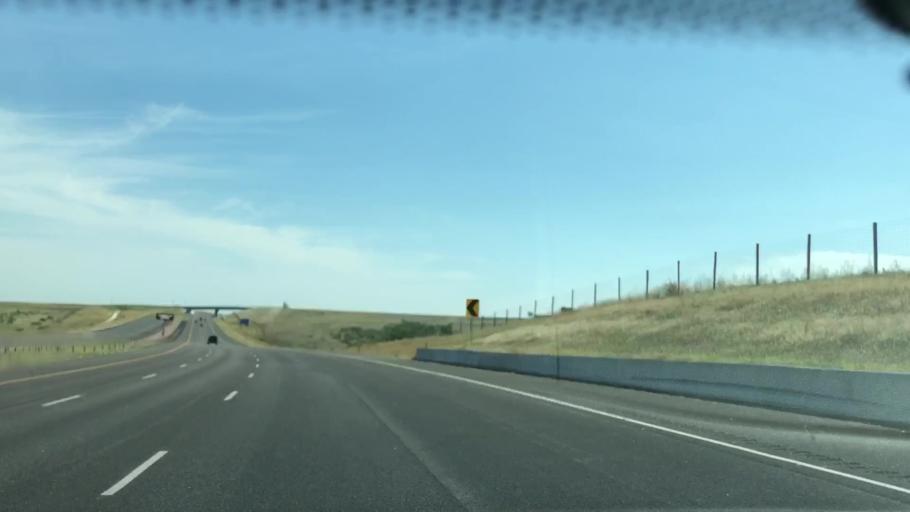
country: US
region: Colorado
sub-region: Douglas County
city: Parker
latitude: 39.5713
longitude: -104.7542
